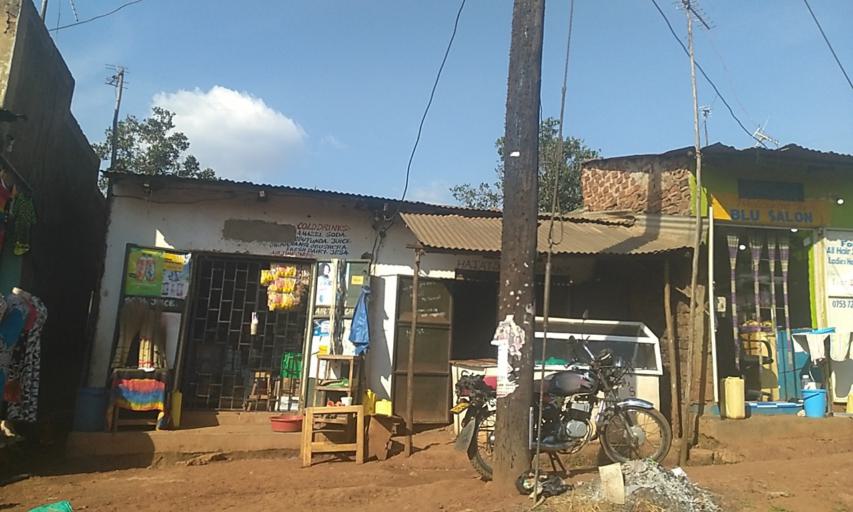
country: UG
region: Central Region
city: Kampala Central Division
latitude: 0.3304
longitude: 32.5306
